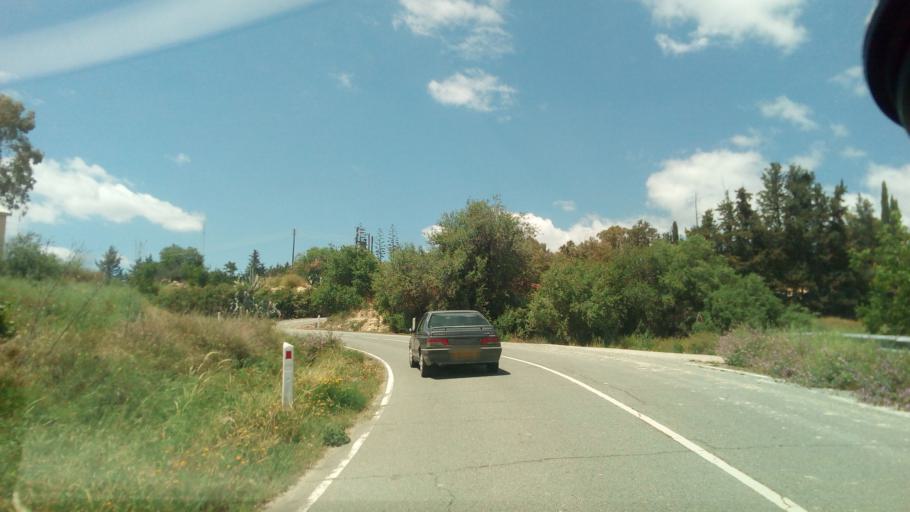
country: CY
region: Limassol
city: Pachna
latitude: 34.8153
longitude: 32.7861
